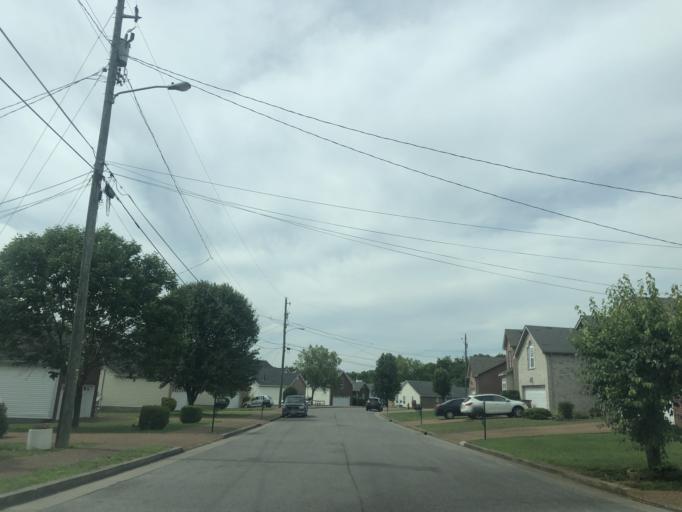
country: US
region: Tennessee
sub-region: Davidson County
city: Nashville
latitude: 36.2133
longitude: -86.8123
